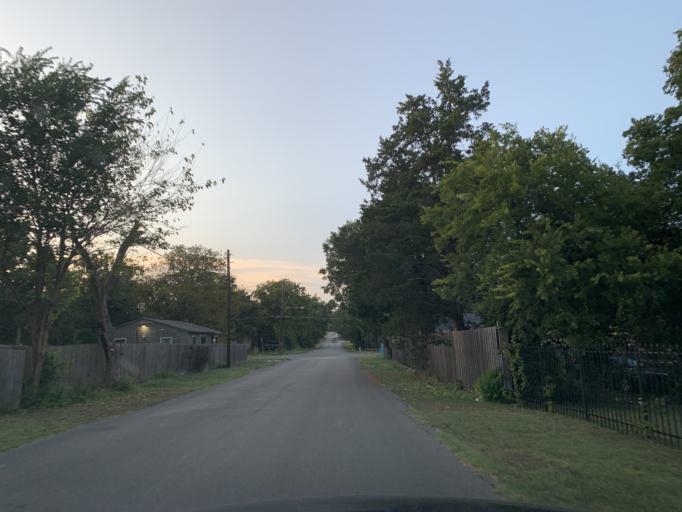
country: US
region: Texas
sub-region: Dallas County
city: Dallas
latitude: 32.7042
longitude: -96.8038
